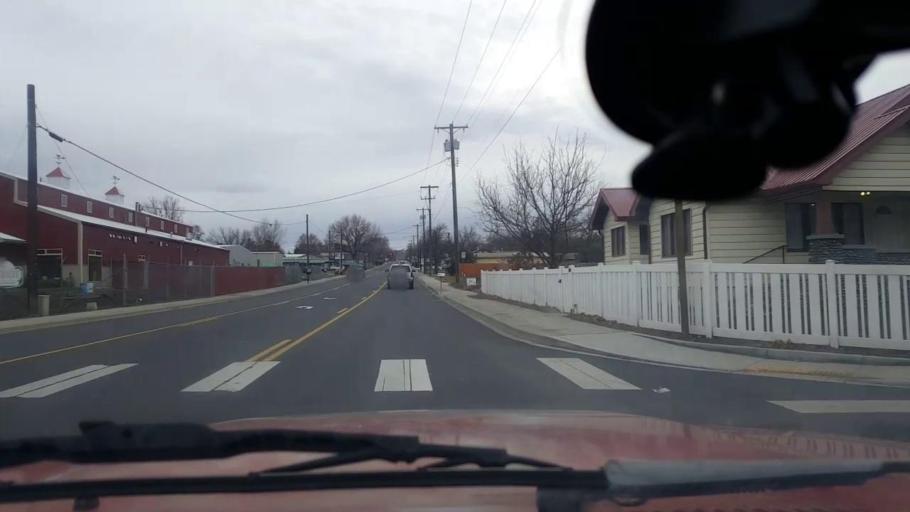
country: US
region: Washington
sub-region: Asotin County
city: West Clarkston-Highland
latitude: 46.4163
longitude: -117.0692
